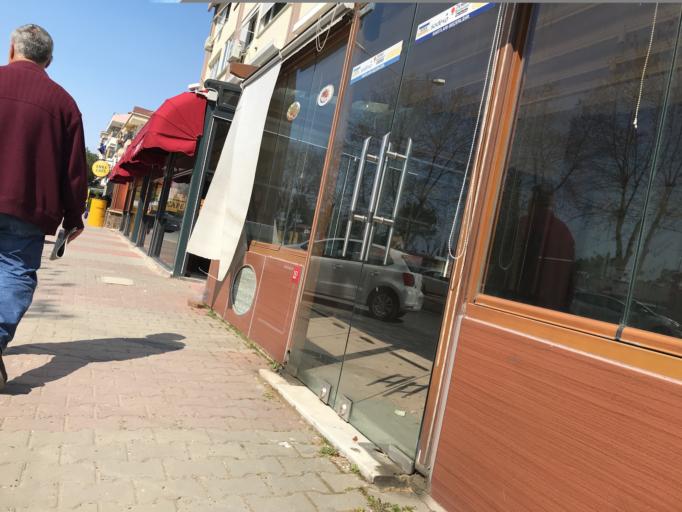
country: TR
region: Istanbul
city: Maltepe
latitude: 40.9220
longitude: 29.1279
